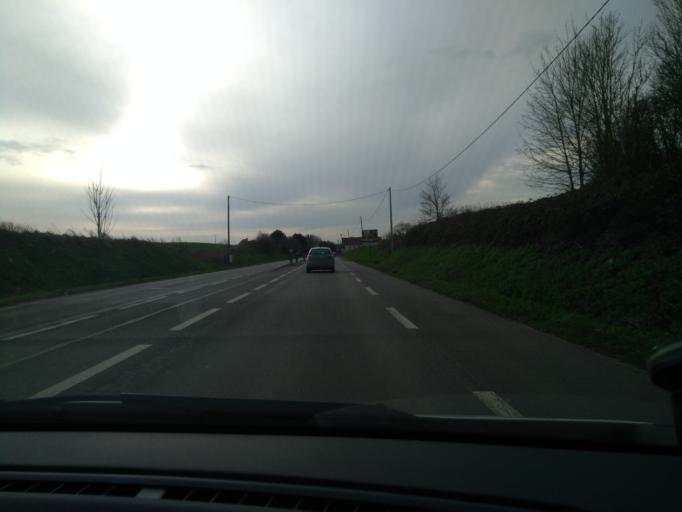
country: FR
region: Nord-Pas-de-Calais
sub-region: Departement du Nord
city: Maubeuge
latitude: 50.3174
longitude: 3.9768
